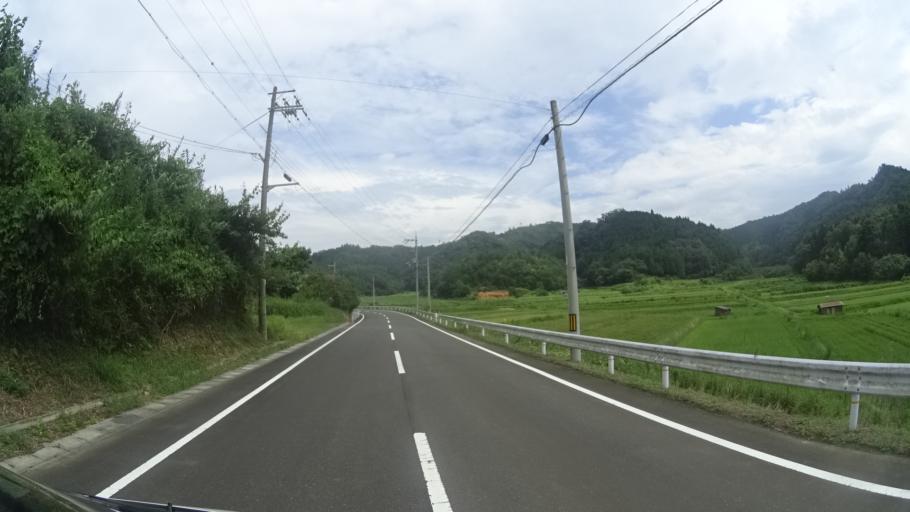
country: JP
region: Kyoto
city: Maizuru
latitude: 35.3557
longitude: 135.3295
